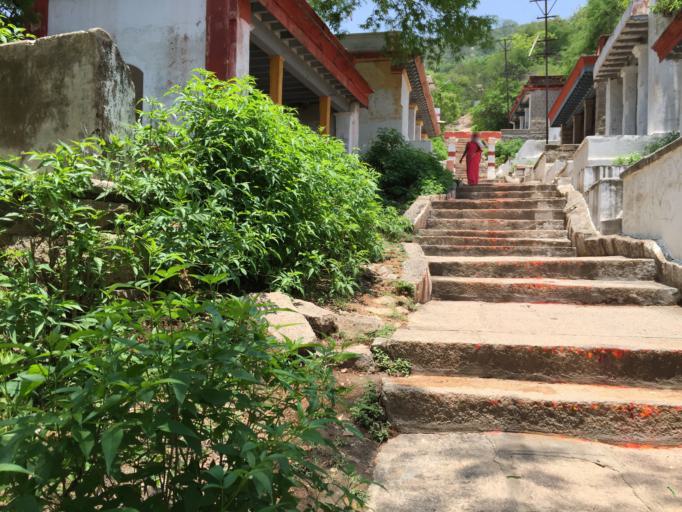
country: IN
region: Karnataka
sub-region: Mysore
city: Mysore
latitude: 12.2840
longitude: 76.6665
